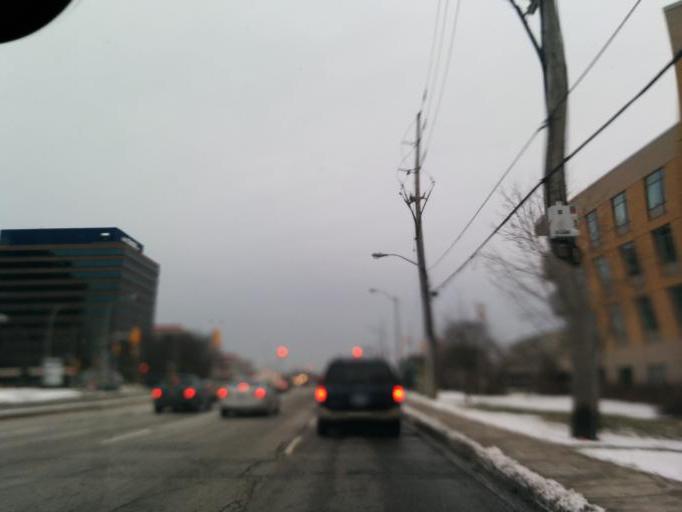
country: CA
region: Ontario
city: Etobicoke
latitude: 43.6442
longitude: -79.5682
